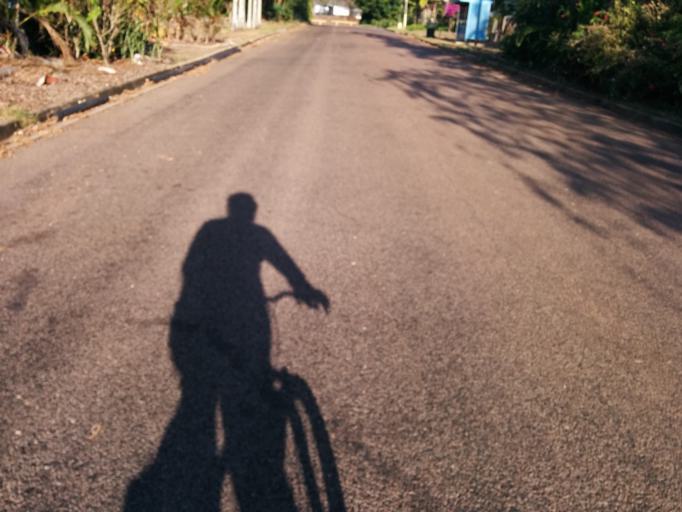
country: AU
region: Northern Territory
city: Alyangula
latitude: -13.8491
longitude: 136.4234
